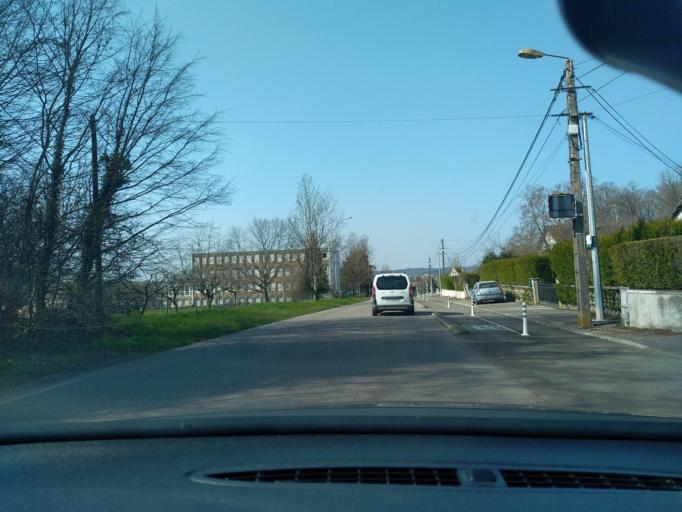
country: FR
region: Franche-Comte
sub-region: Departement du Jura
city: Dole
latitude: 47.0700
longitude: 5.5042
